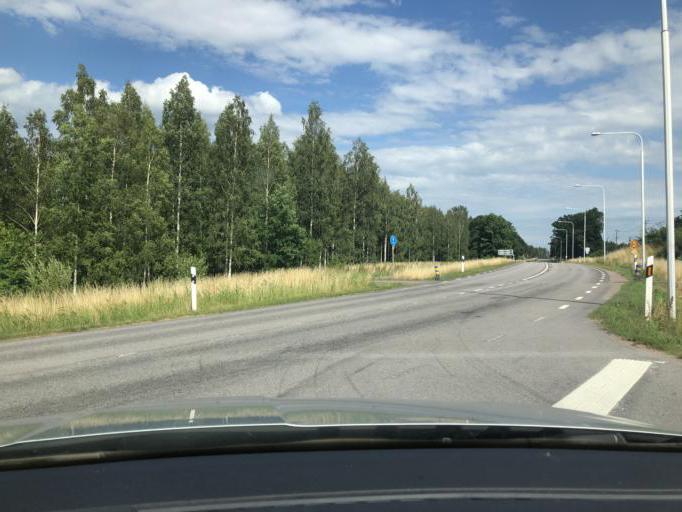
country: SE
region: OEstergoetland
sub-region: Mjolby Kommun
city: Mjolby
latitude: 58.3365
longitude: 15.1659
